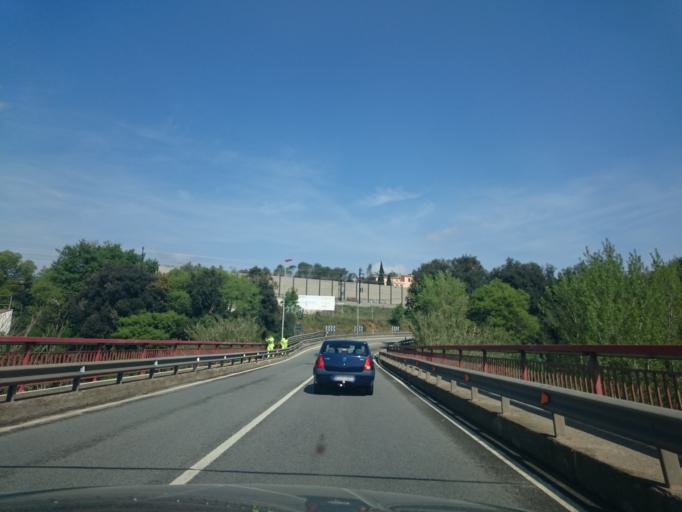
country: ES
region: Catalonia
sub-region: Provincia de Girona
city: Bascara
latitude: 42.1637
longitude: 2.9095
